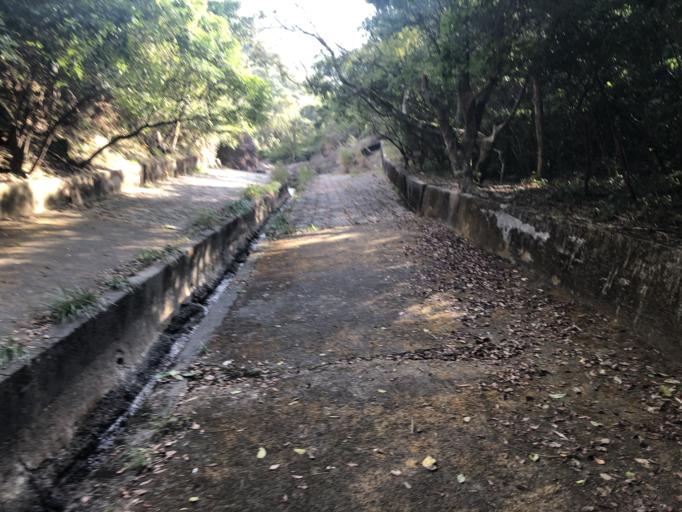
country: HK
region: Wanchai
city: Wan Chai
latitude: 22.2754
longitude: 114.2137
